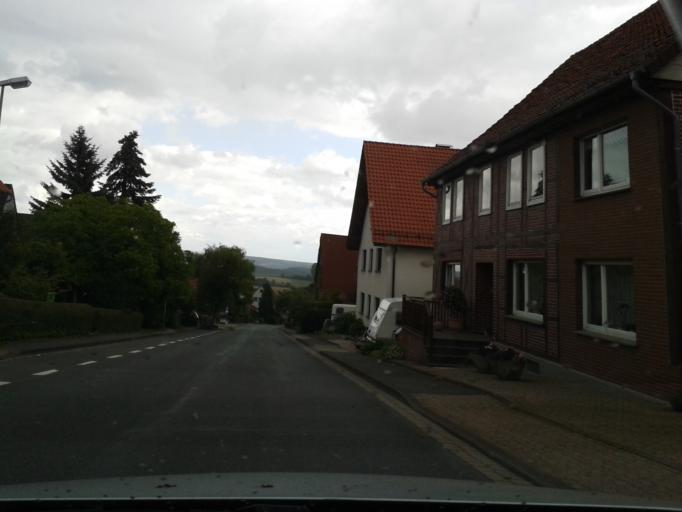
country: DE
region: North Rhine-Westphalia
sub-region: Regierungsbezirk Detmold
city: Barntrup
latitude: 51.9617
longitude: 9.1717
